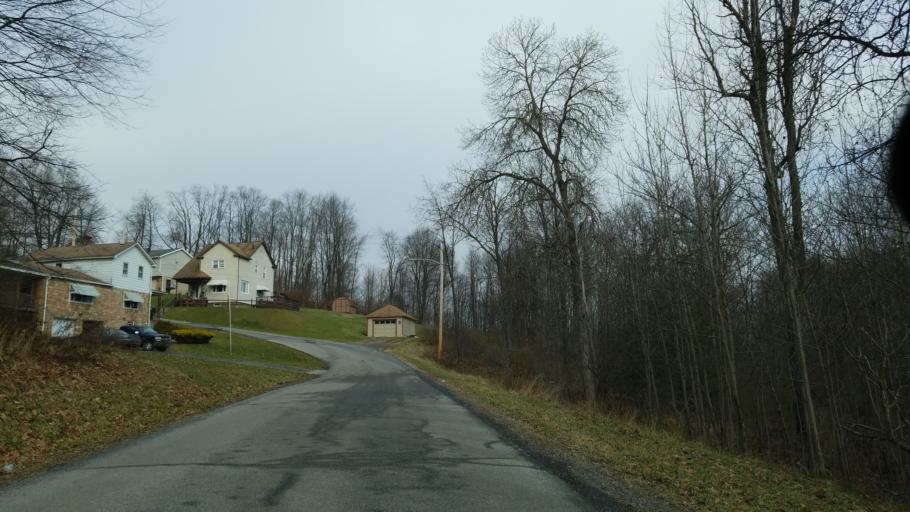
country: US
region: Pennsylvania
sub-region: Clearfield County
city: Sandy
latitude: 41.1255
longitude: -78.7795
